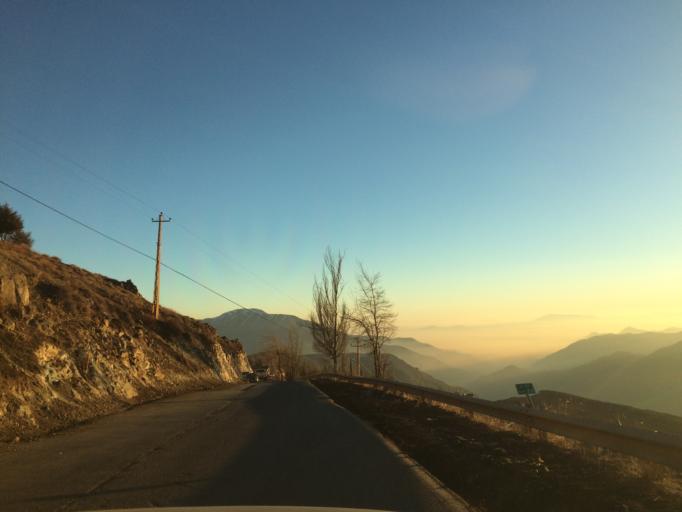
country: CL
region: Santiago Metropolitan
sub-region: Provincia de Santiago
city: Villa Presidente Frei, Nunoa, Santiago, Chile
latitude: -33.3474
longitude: -70.3055
